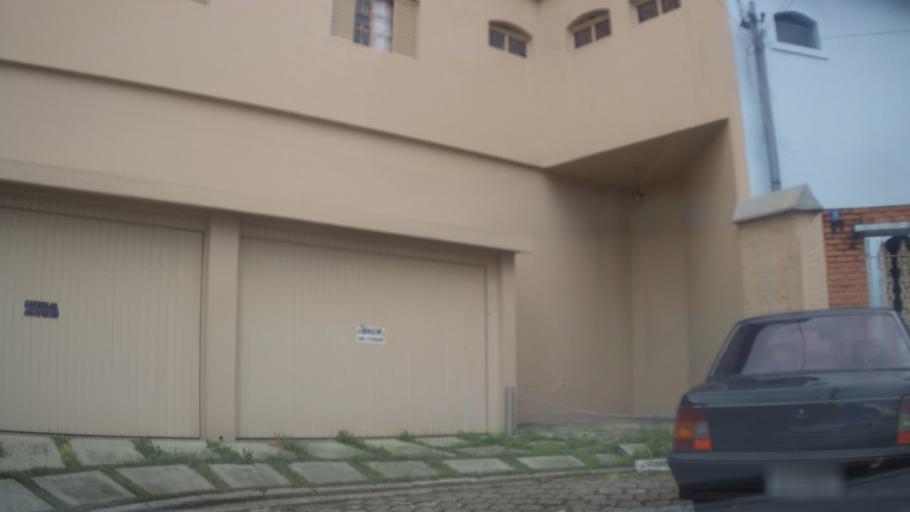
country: BR
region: Sao Paulo
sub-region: Guarulhos
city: Guarulhos
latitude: -23.5024
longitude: -46.5521
